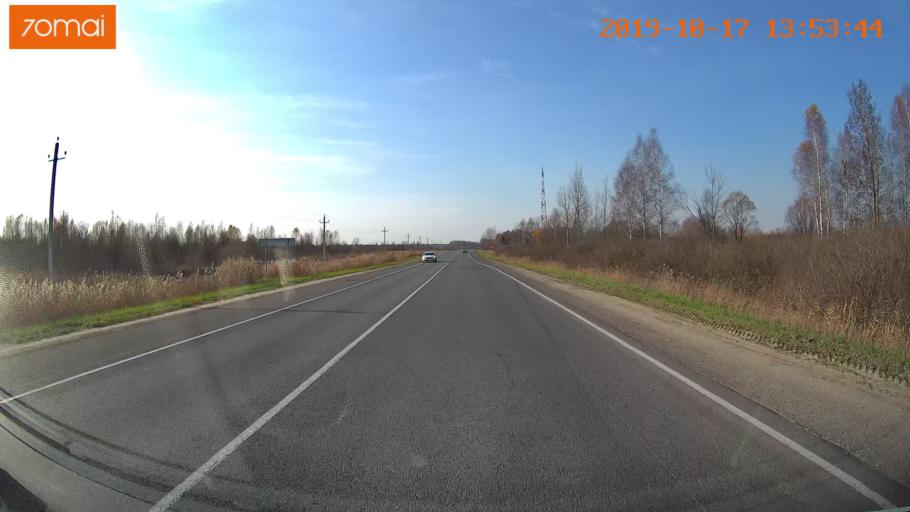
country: RU
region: Rjazan
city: Spas-Klepiki
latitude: 55.1432
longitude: 40.3336
